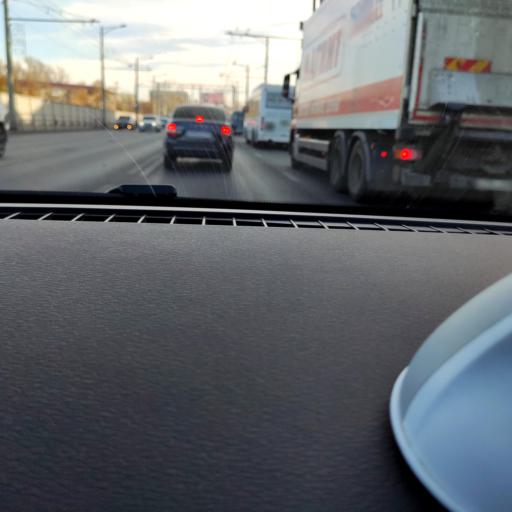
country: RU
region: Samara
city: Samara
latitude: 53.2035
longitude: 50.1553
